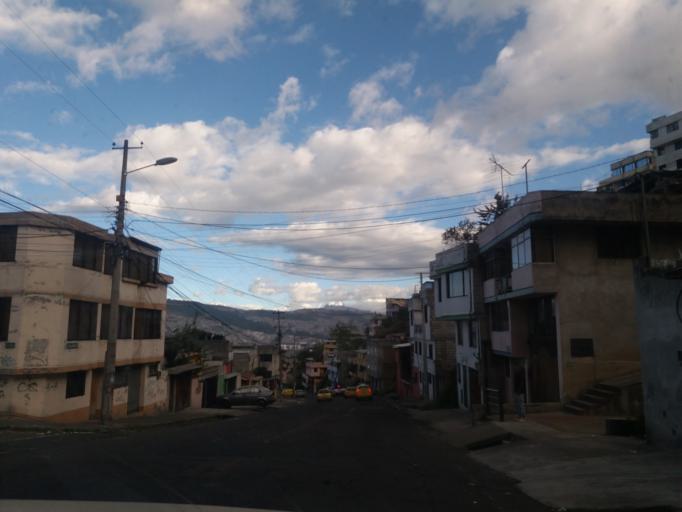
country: EC
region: Pichincha
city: Quito
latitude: -0.2308
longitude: -78.5333
